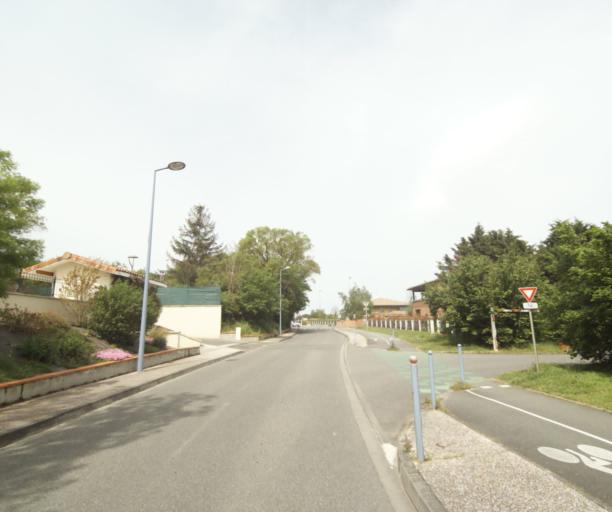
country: FR
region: Midi-Pyrenees
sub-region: Departement de la Haute-Garonne
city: Auzeville-Tolosane
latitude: 43.5222
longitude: 1.4904
